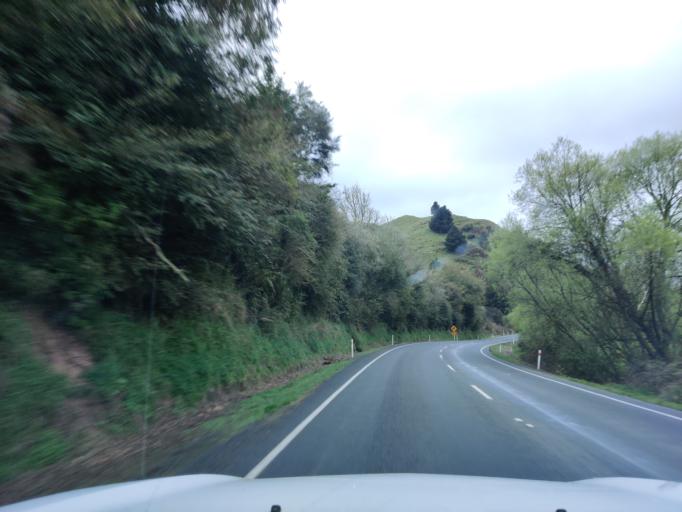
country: NZ
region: Waikato
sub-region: Otorohanga District
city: Otorohanga
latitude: -38.5996
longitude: 175.2171
